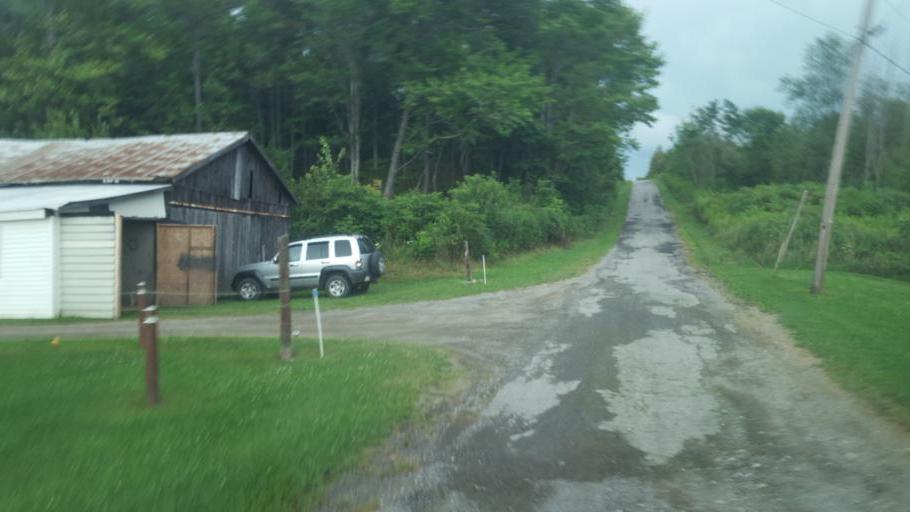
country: US
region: Pennsylvania
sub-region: Clarion County
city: Knox
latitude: 41.1465
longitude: -79.5120
